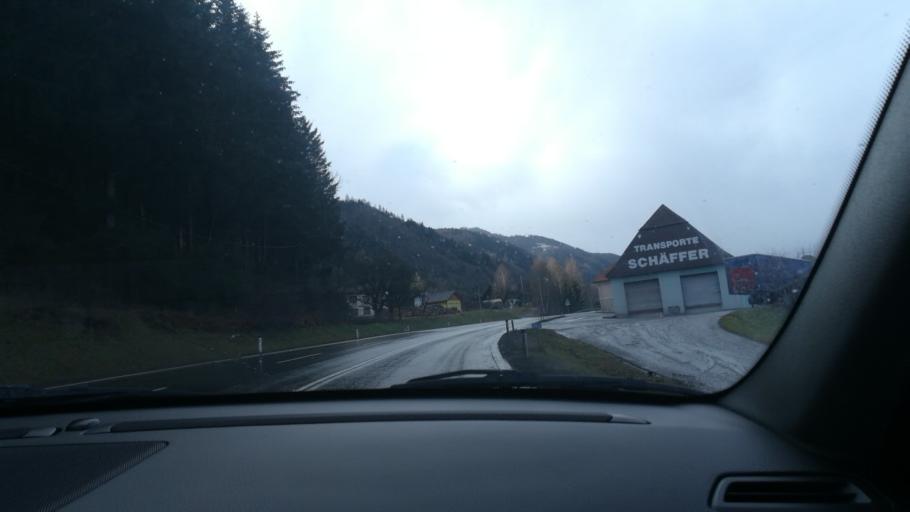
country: AT
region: Styria
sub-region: Politischer Bezirk Murtal
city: Sankt Georgen ob Judenburg
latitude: 47.2011
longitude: 14.5322
